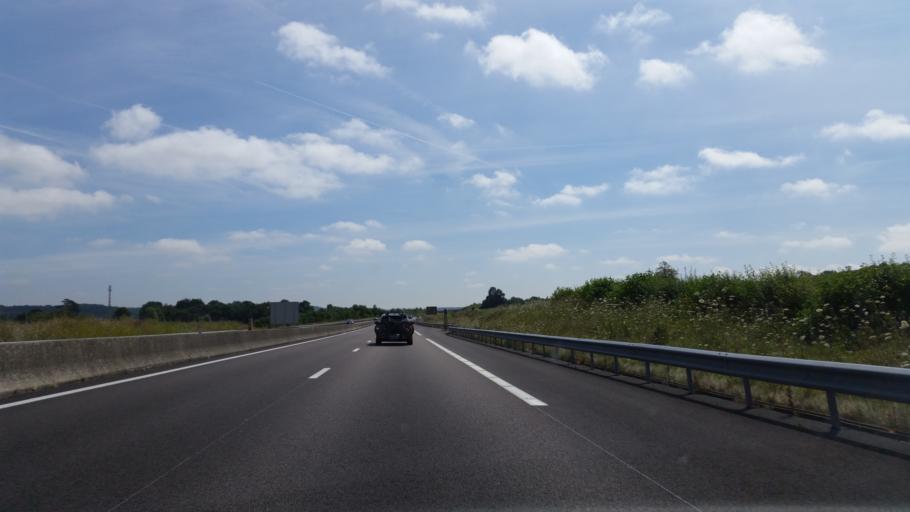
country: FR
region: Haute-Normandie
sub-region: Departement de la Seine-Maritime
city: Neufchatel-en-Bray
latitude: 49.7476
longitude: 1.5188
